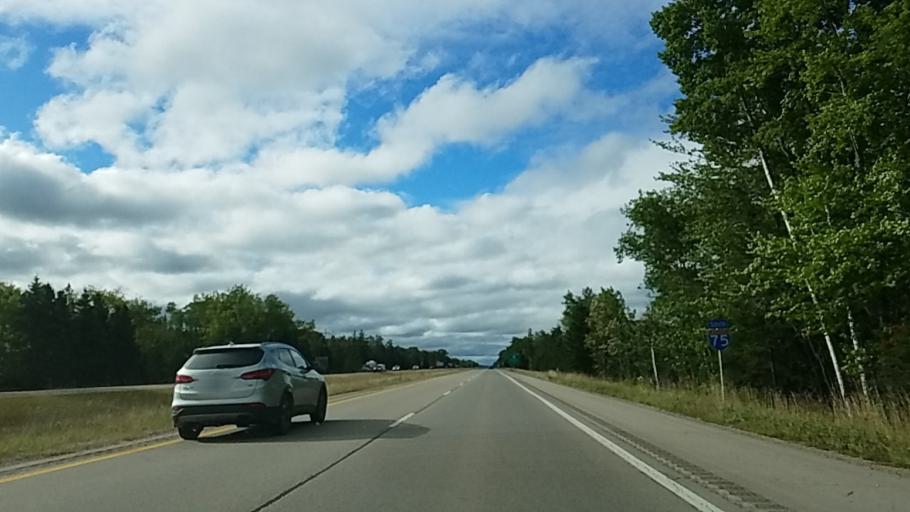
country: US
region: Michigan
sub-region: Mackinac County
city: Saint Ignace
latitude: 45.7539
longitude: -84.7290
